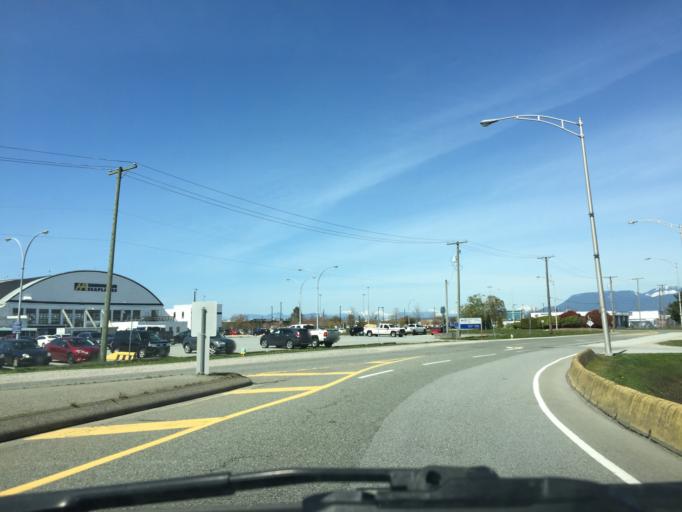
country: CA
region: British Columbia
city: Richmond
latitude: 49.1779
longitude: -123.1669
